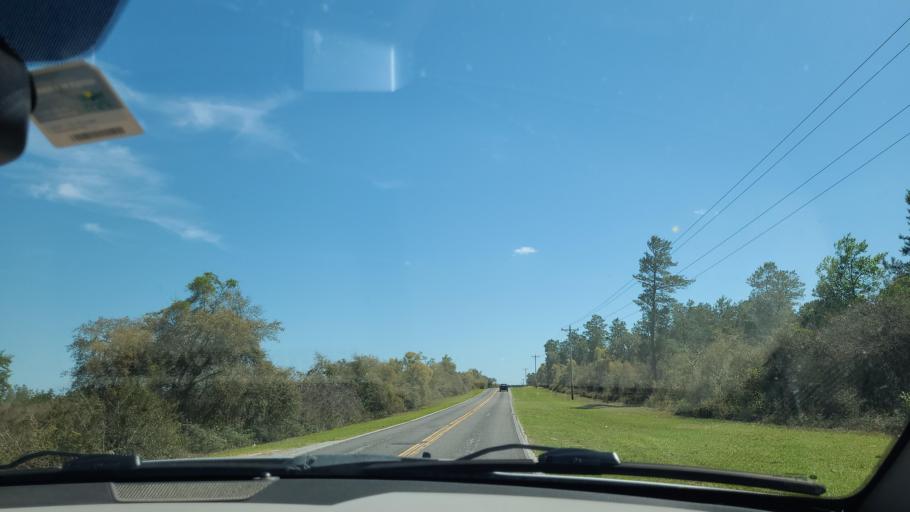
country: US
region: Florida
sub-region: Marion County
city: Citra
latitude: 29.4018
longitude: -81.8950
